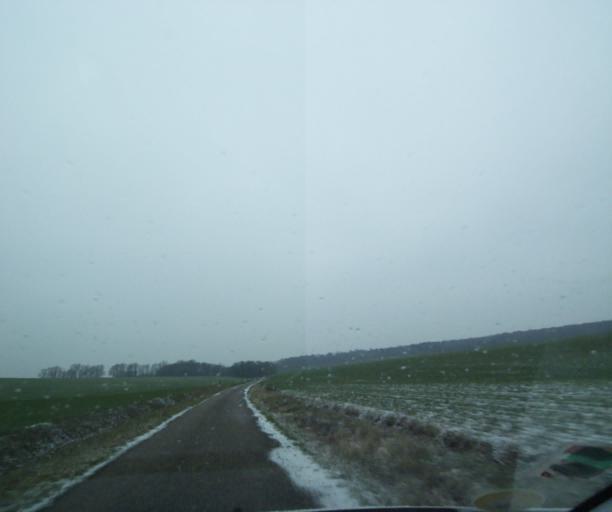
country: FR
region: Champagne-Ardenne
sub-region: Departement de la Haute-Marne
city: Wassy
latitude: 48.4628
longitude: 5.0239
